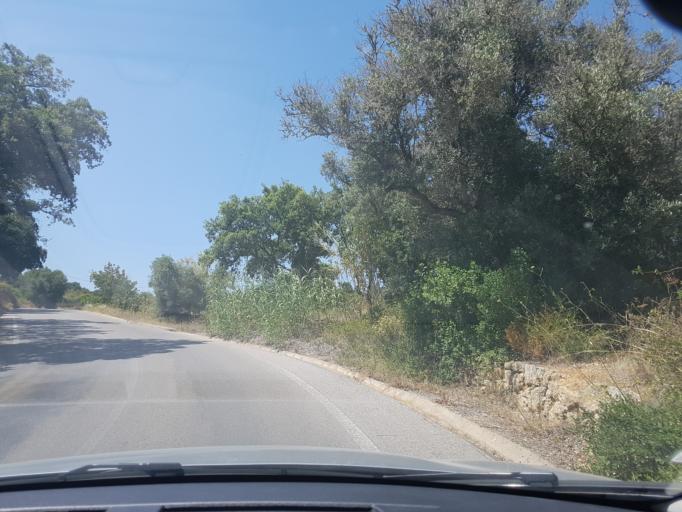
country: PT
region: Faro
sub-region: Lagoa
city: Carvoeiro
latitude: 37.1043
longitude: -8.4292
